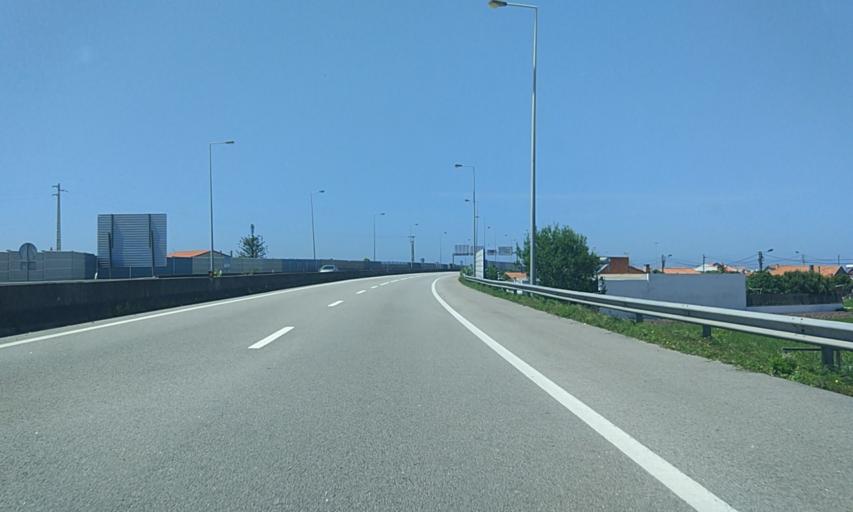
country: PT
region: Aveiro
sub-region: Ilhavo
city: Gafanha da Encarnacao
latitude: 40.6259
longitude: -8.7258
